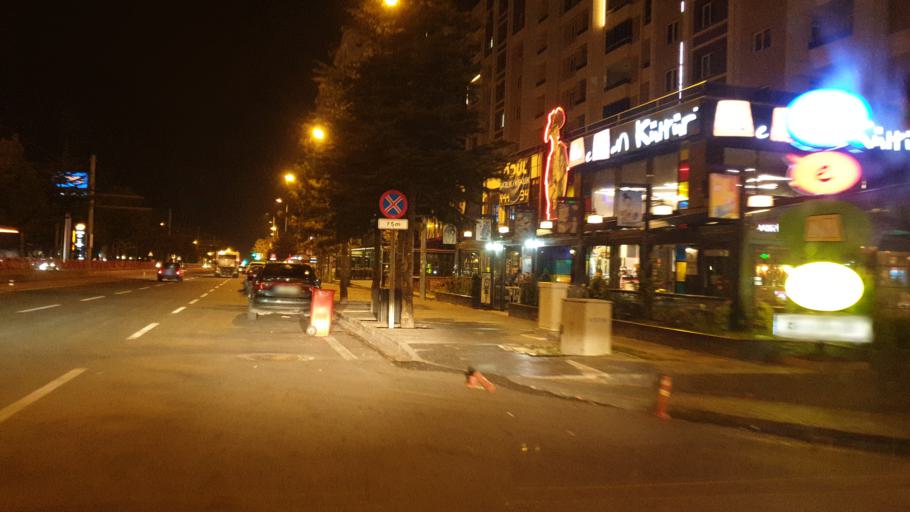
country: TR
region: Kayseri
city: Talas
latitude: 38.6947
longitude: 35.5433
